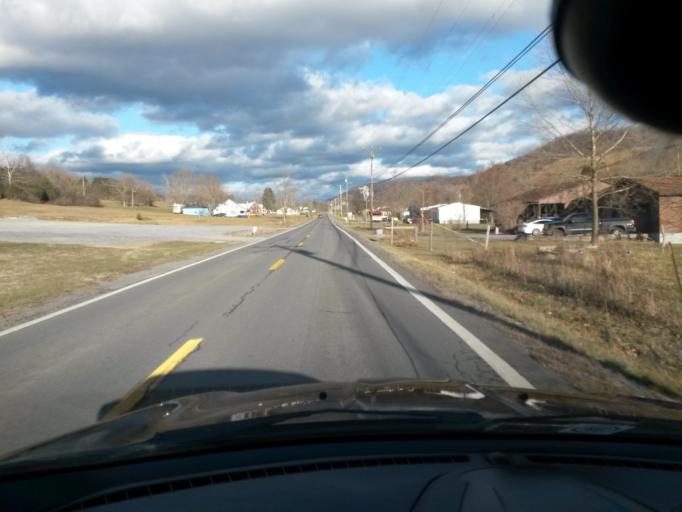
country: US
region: Virginia
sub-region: Giles County
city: Pearisburg
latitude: 37.4431
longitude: -80.6868
